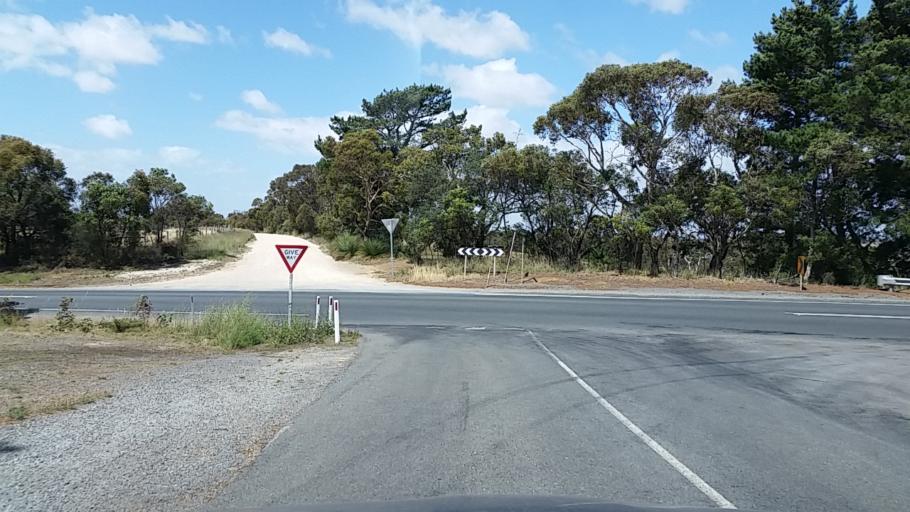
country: AU
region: South Australia
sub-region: Alexandrina
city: Port Elliot
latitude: -35.4539
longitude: 138.6435
